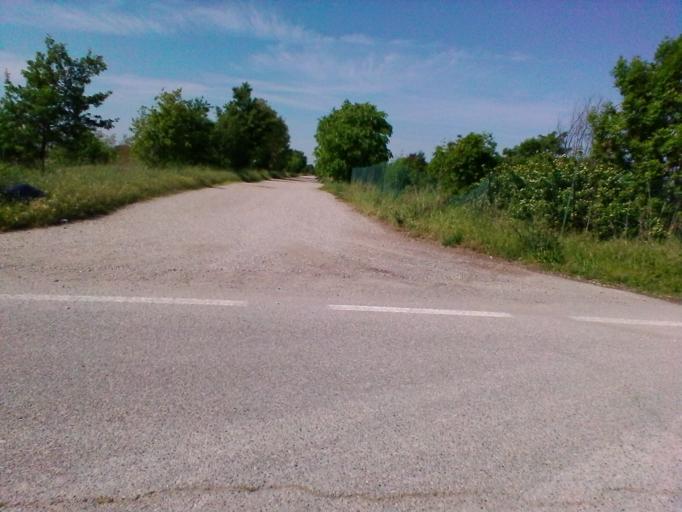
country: IT
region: Lombardy
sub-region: Provincia di Mantova
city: Roverbella
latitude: 45.2869
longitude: 10.7366
